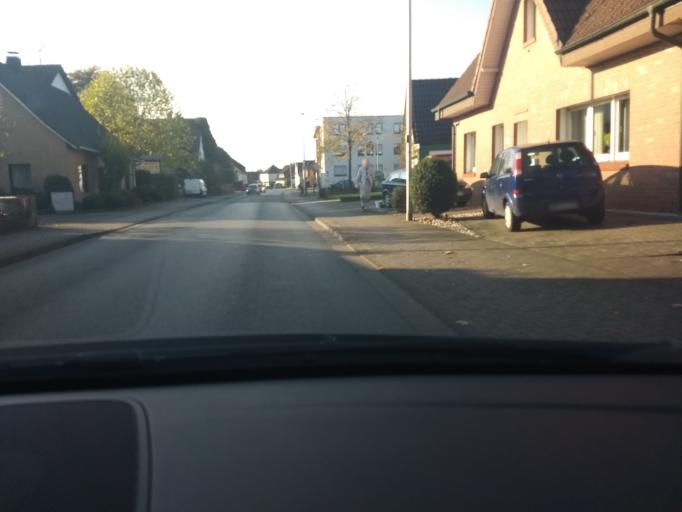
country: DE
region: North Rhine-Westphalia
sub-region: Regierungsbezirk Munster
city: Borken
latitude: 51.8604
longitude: 6.8607
